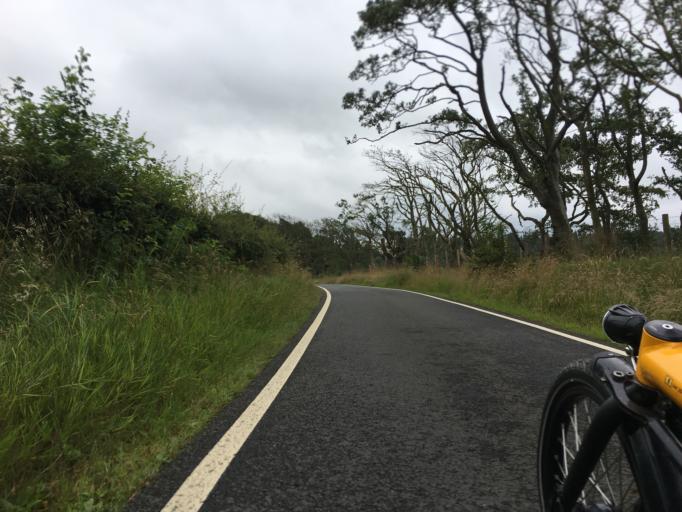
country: GB
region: Scotland
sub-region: West Lothian
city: West Calder
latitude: 55.8457
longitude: -3.5310
